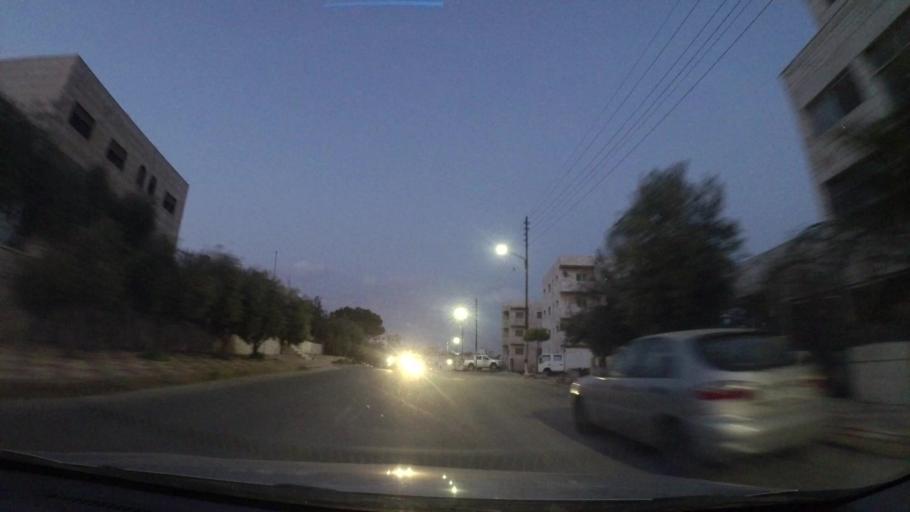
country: JO
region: Amman
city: Al Quwaysimah
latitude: 31.8915
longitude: 35.9271
